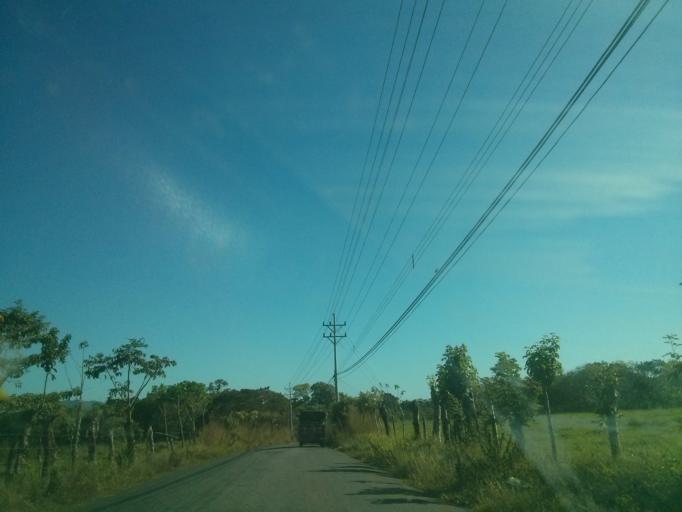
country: CR
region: Puntarenas
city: Paquera
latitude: 9.6841
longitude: -85.1116
